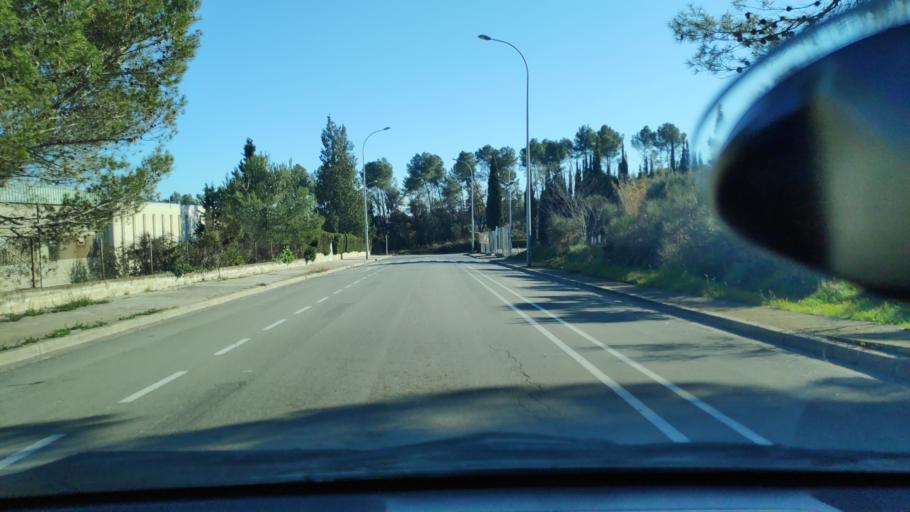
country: ES
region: Catalonia
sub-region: Provincia de Barcelona
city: Sant Quirze del Valles
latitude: 41.5205
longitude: 2.0919
